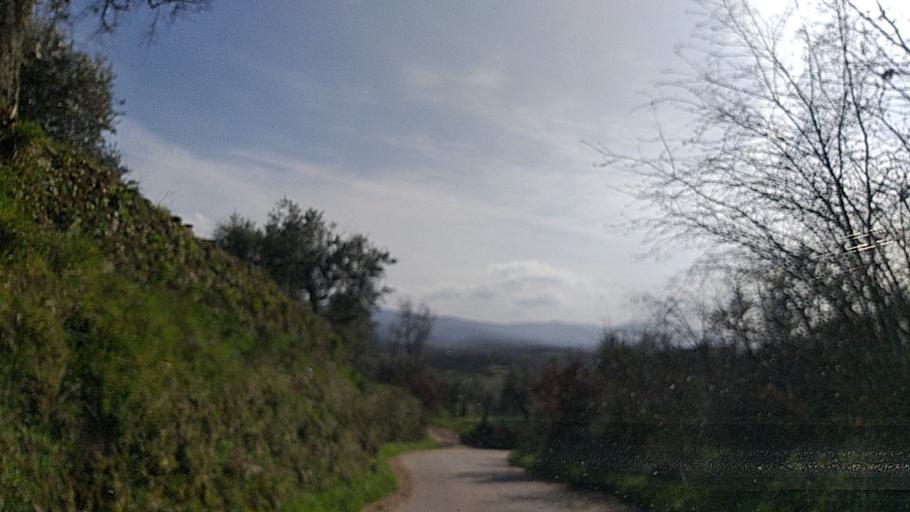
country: PT
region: Guarda
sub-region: Celorico da Beira
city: Celorico da Beira
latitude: 40.6548
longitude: -7.4117
